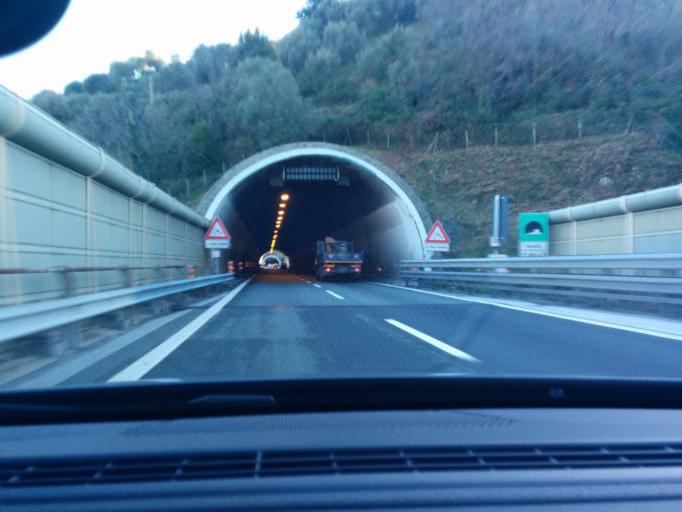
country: IT
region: Liguria
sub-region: Provincia di Savona
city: Celle Ligure
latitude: 44.3469
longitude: 8.5418
